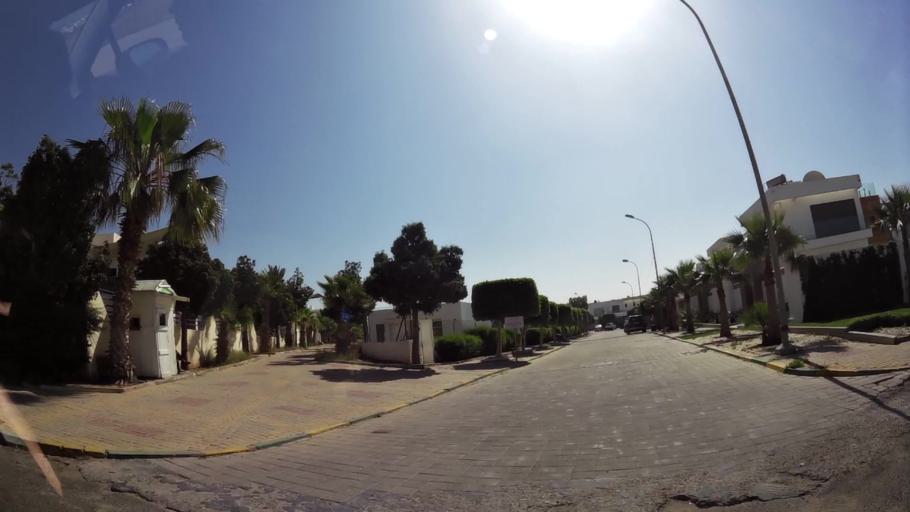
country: MA
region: Souss-Massa-Draa
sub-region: Agadir-Ida-ou-Tnan
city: Agadir
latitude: 30.4378
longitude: -9.5803
